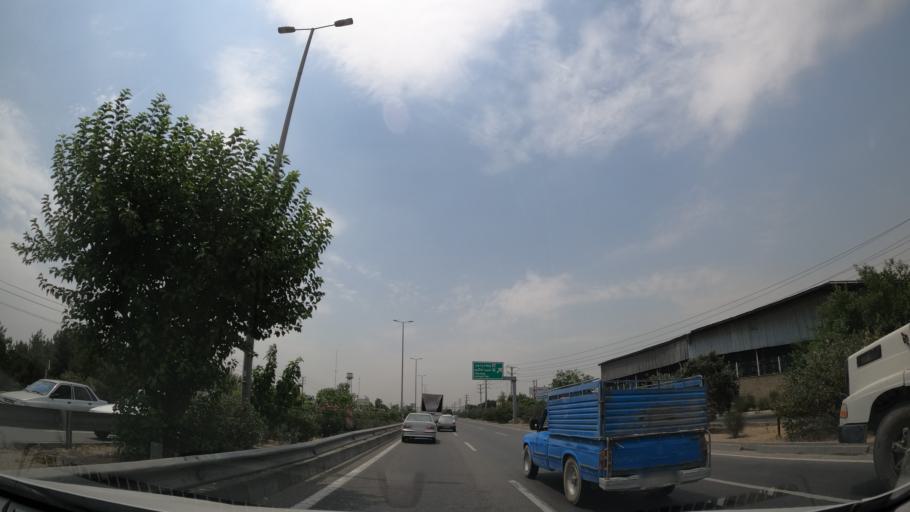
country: IR
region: Tehran
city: Shahr-e Qods
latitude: 35.7062
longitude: 51.1736
